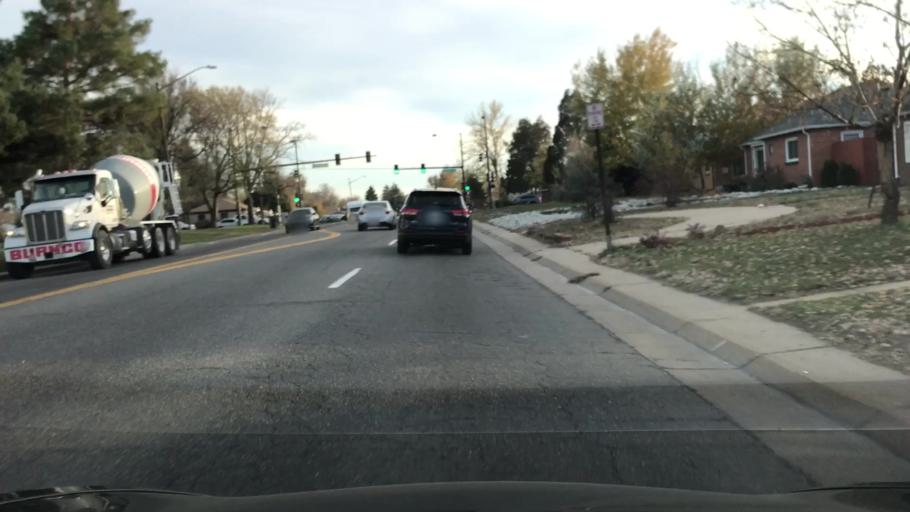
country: US
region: Colorado
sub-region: Arapahoe County
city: Glendale
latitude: 39.7519
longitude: -104.9035
